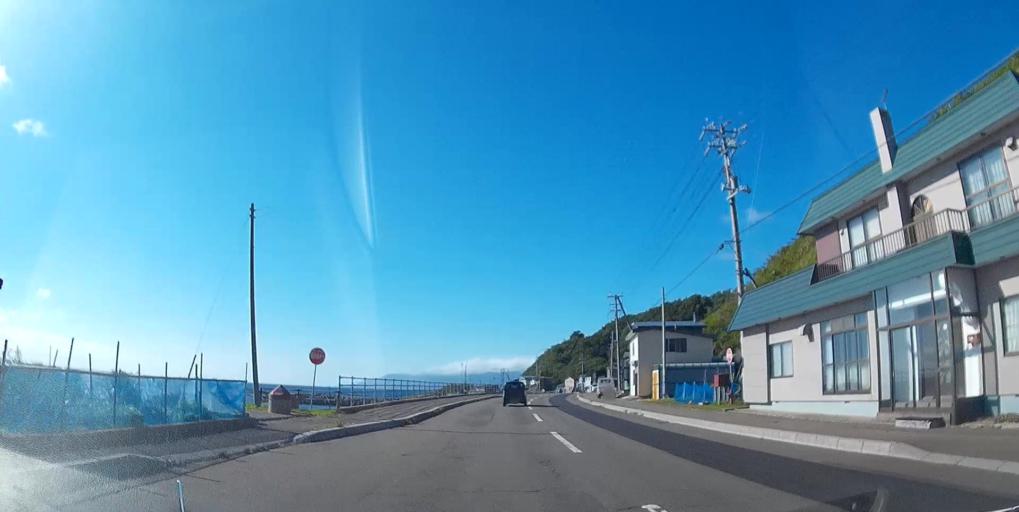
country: JP
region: Hokkaido
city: Kamiiso
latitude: 42.1453
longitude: 139.9168
